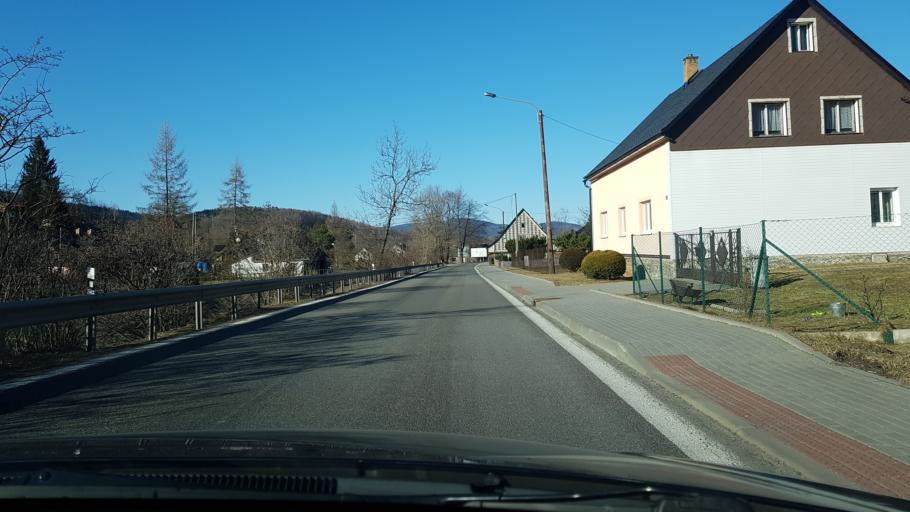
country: CZ
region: Olomoucky
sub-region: Okres Jesenik
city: Jesenik
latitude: 50.1646
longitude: 17.1959
